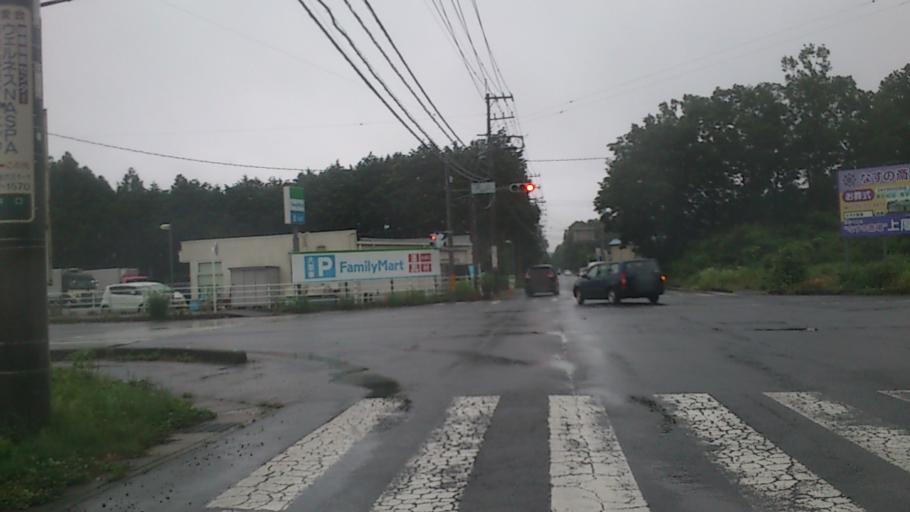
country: JP
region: Tochigi
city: Otawara
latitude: 36.9188
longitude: 139.9733
